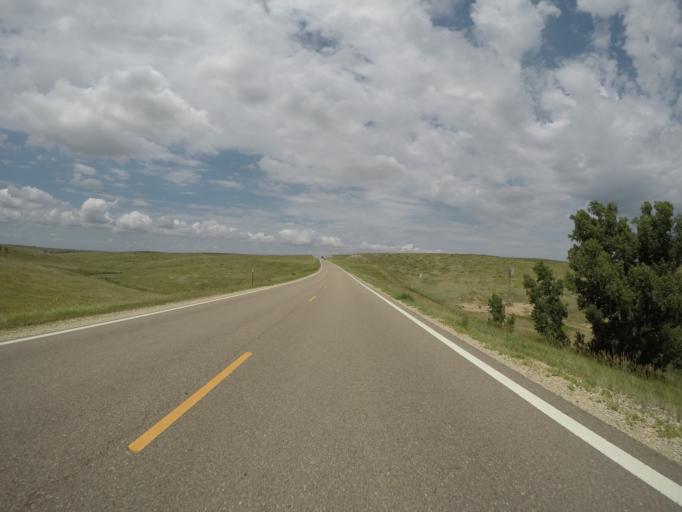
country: US
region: Kansas
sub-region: Rawlins County
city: Atwood
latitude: 39.7537
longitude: -101.0471
